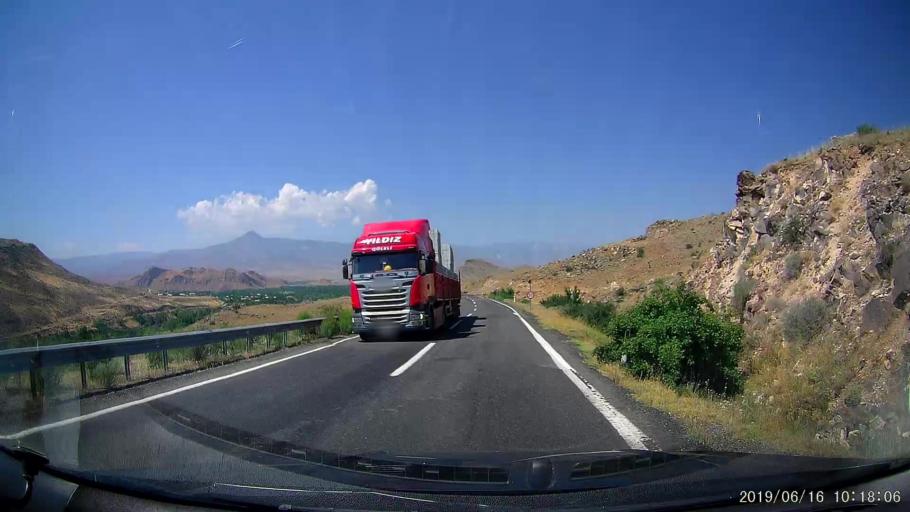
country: TR
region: Igdir
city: Tuzluca
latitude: 40.1634
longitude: 43.6726
